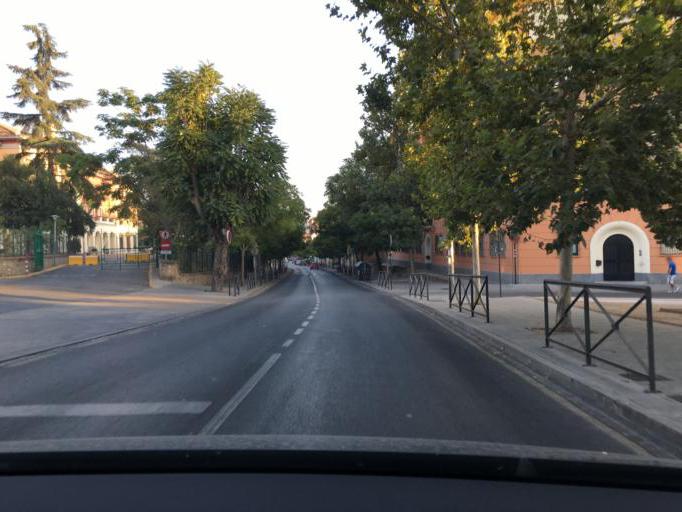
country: ES
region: Andalusia
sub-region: Provincia de Granada
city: Granada
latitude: 37.1939
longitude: -3.6045
